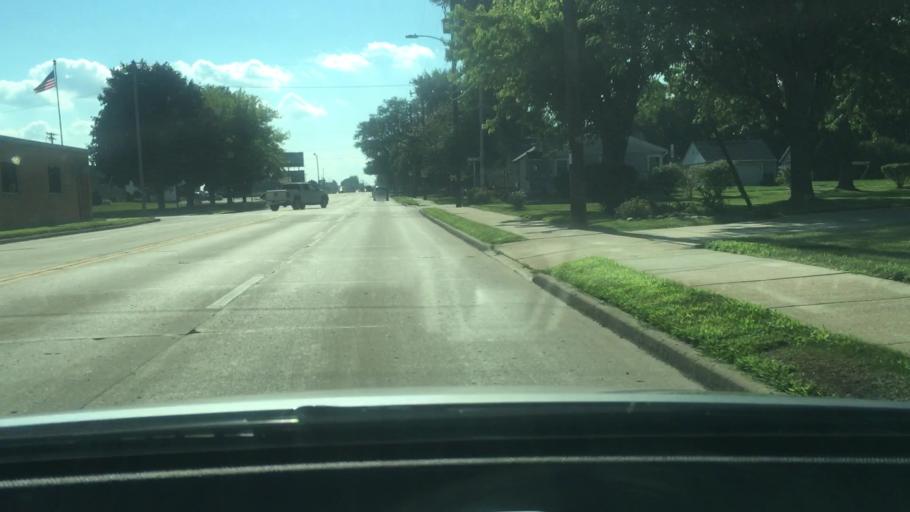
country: US
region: Wisconsin
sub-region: Winnebago County
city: Oshkosh
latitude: 43.9959
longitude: -88.5456
